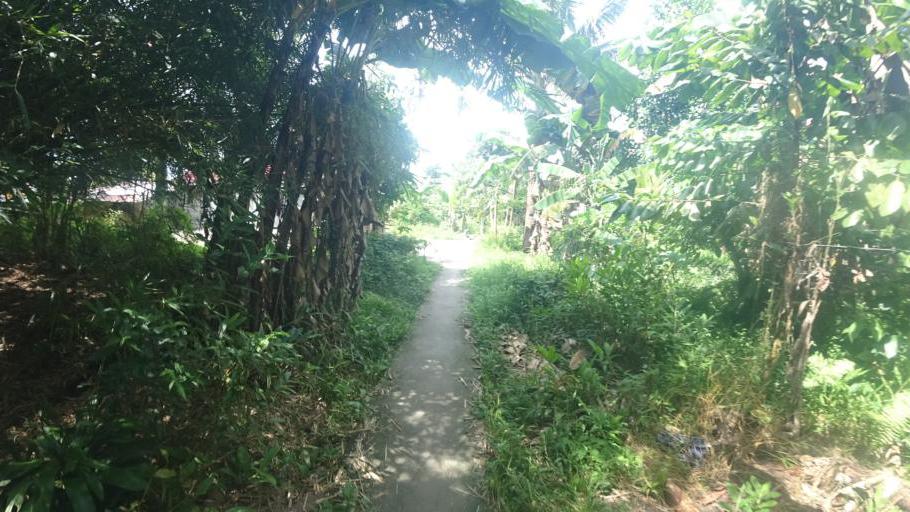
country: PH
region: Eastern Visayas
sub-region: Province of Leyte
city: Jaro
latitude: 11.2029
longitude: 124.8081
